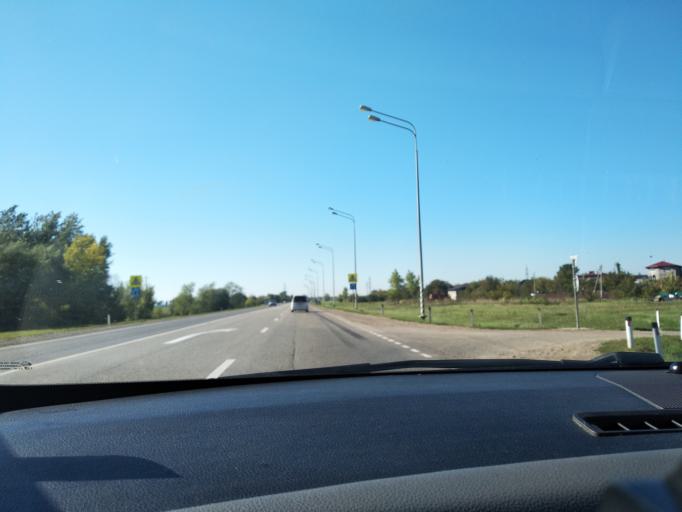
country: RU
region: Krasnodarskiy
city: Agronom
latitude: 45.1646
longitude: 39.0855
